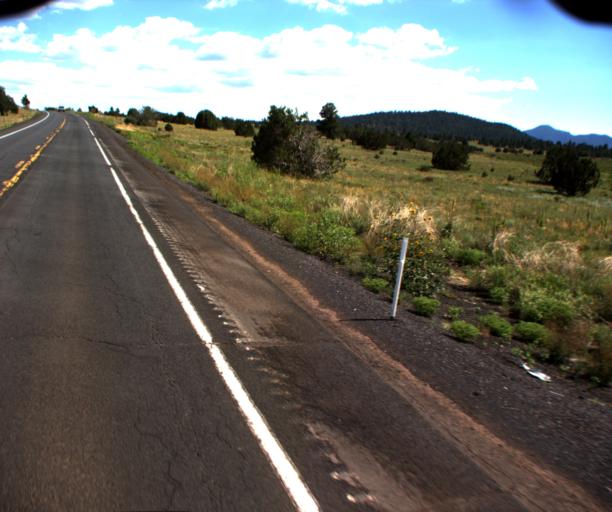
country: US
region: Arizona
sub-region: Coconino County
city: Williams
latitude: 35.3225
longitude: -112.1530
